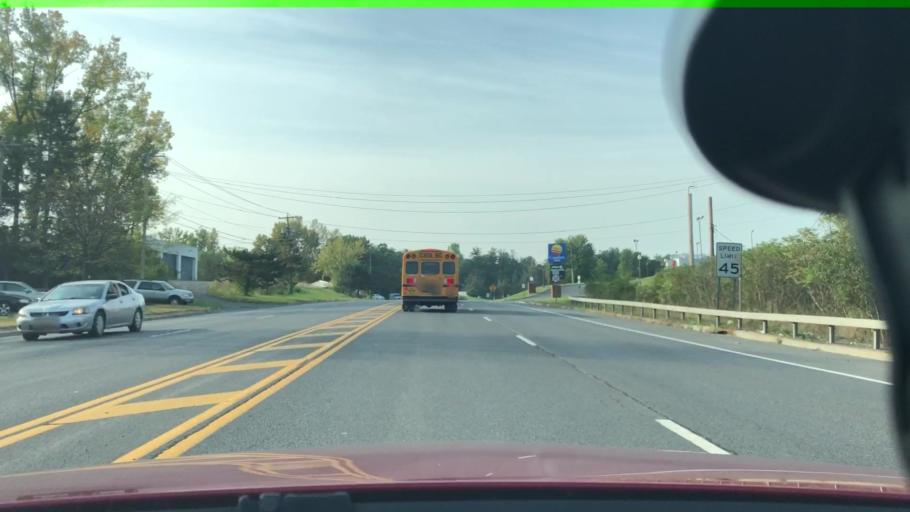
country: US
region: New York
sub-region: Albany County
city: Albany
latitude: 42.6238
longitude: -73.7772
